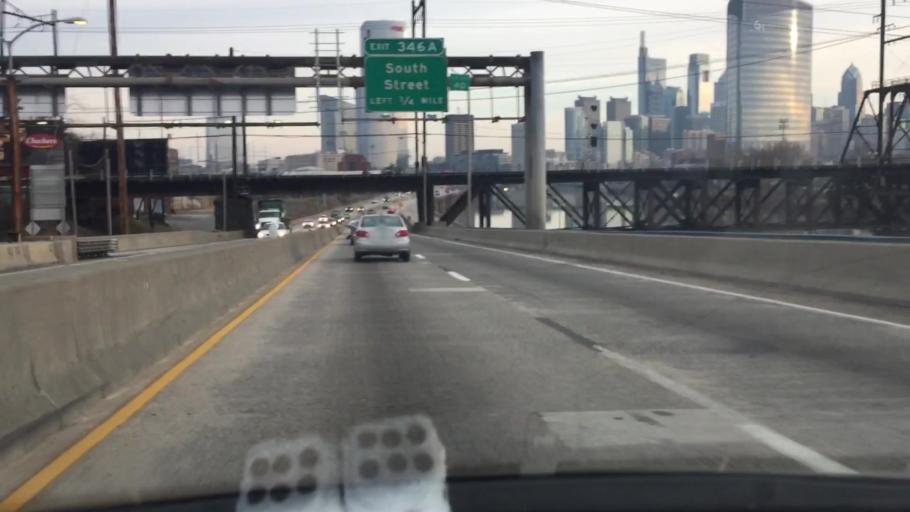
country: US
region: Pennsylvania
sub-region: Philadelphia County
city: Philadelphia
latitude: 39.9429
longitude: -75.1931
